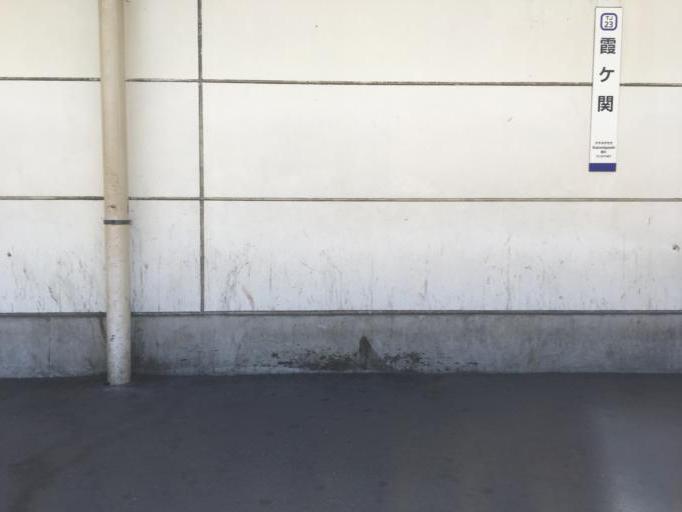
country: JP
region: Saitama
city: Kawagoe
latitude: 35.9253
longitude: 139.4440
